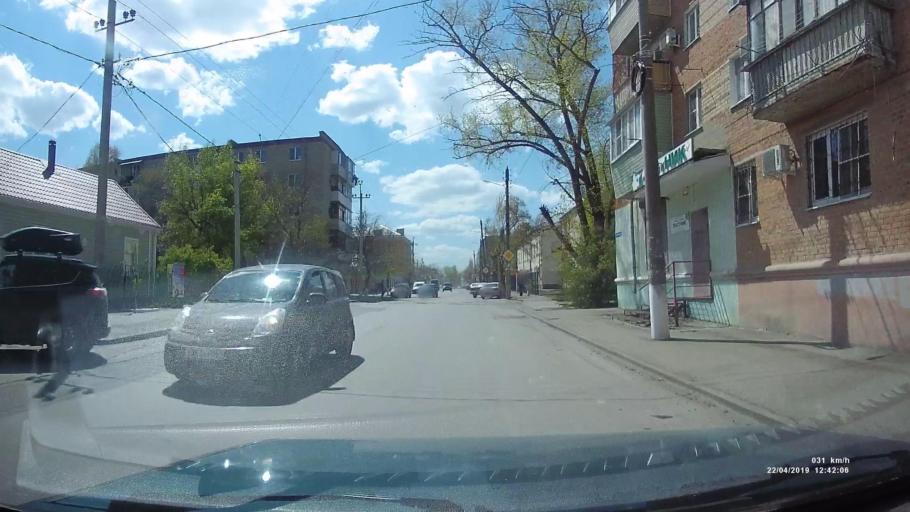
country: RU
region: Rostov
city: Azov
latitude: 47.1059
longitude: 39.4281
